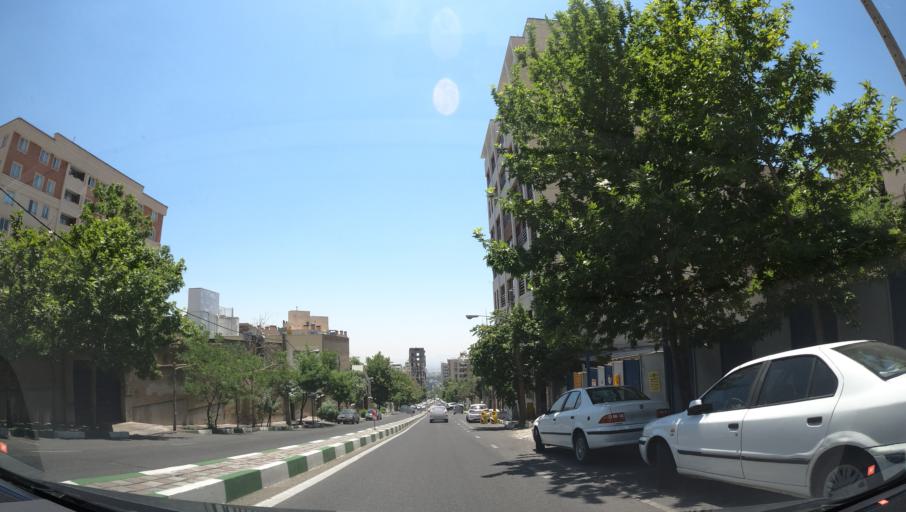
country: IR
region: Tehran
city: Tajrish
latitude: 35.8104
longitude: 51.3999
